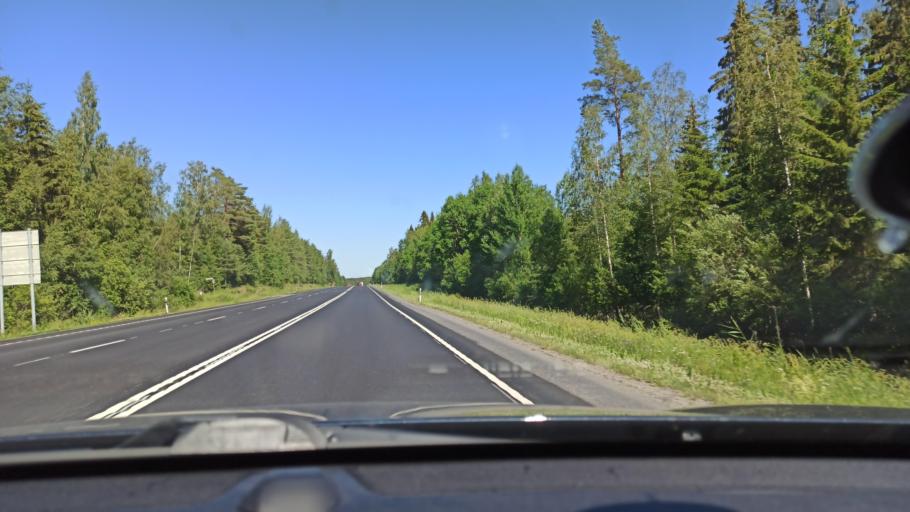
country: FI
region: Ostrobothnia
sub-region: Vaasa
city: Oravais
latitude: 63.2742
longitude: 22.3260
